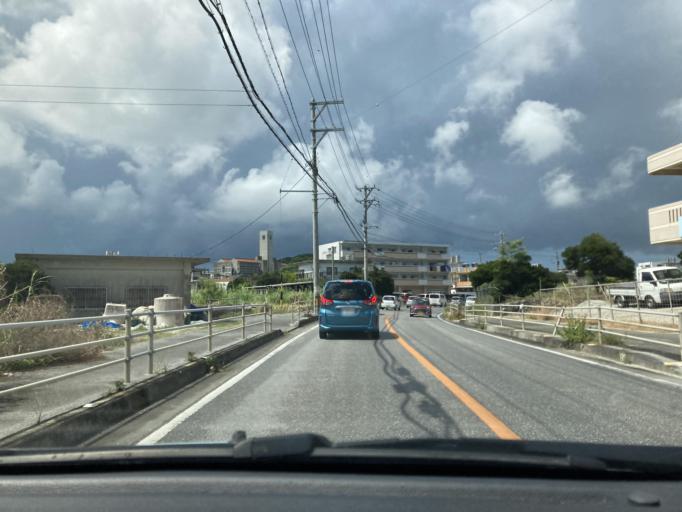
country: JP
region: Okinawa
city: Tomigusuku
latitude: 26.1756
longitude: 127.7493
